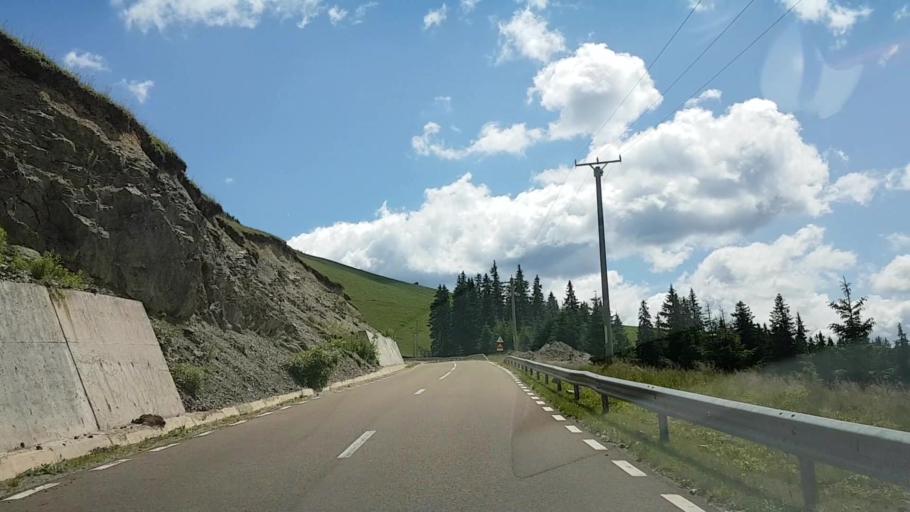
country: RO
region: Suceava
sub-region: Comuna Sadova
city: Sadova
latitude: 47.4591
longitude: 25.5288
